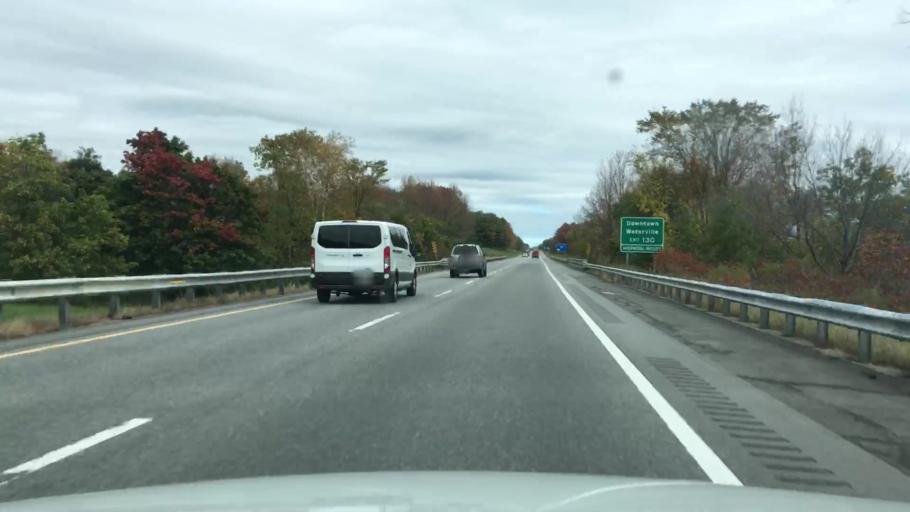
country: US
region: Maine
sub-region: Kennebec County
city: Oakland
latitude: 44.5240
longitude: -69.6962
